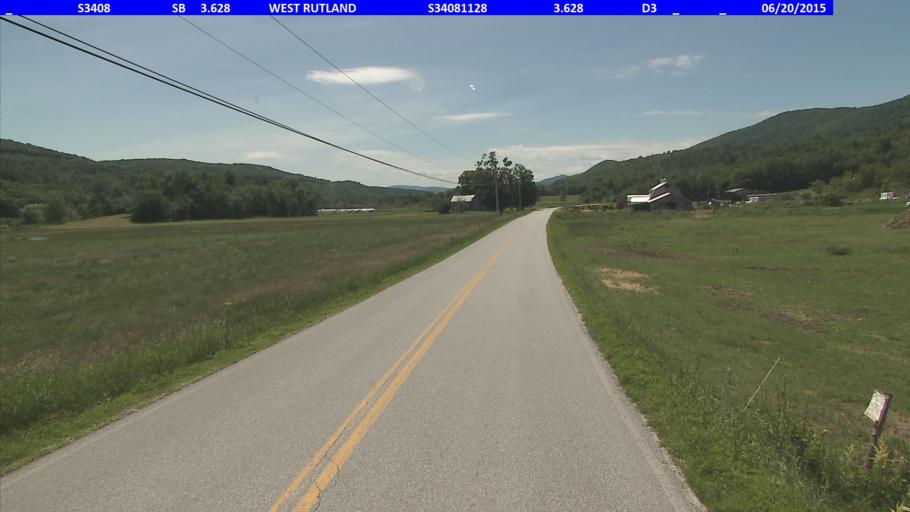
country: US
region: Vermont
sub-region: Rutland County
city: West Rutland
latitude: 43.6610
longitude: -73.0738
